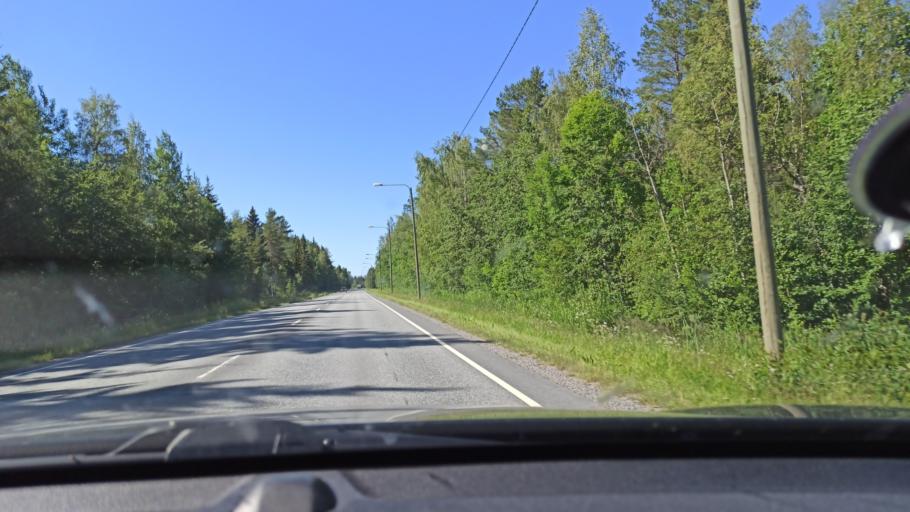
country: FI
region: Ostrobothnia
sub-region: Jakobstadsregionen
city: Jakobstad
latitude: 63.6466
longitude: 22.7288
